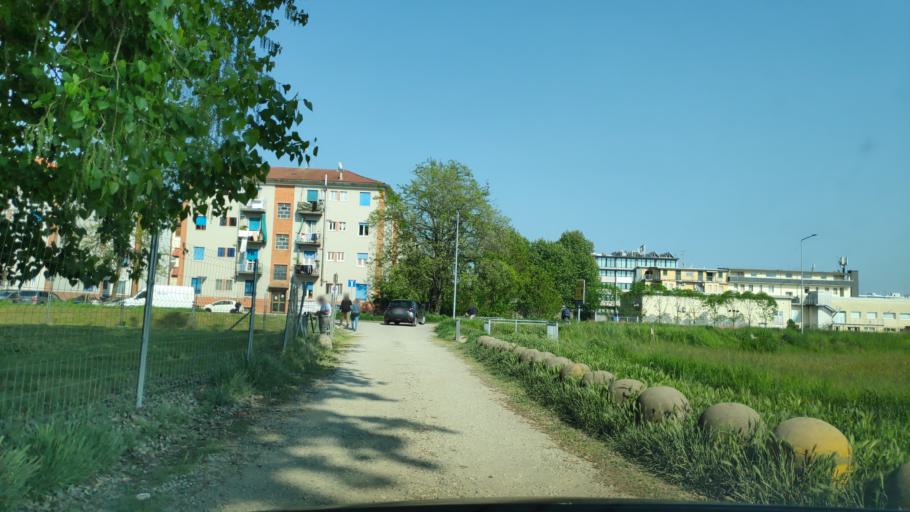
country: IT
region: Lombardy
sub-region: Citta metropolitana di Milano
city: Novegro-Tregarezzo-San Felice
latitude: 45.4683
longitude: 9.2770
